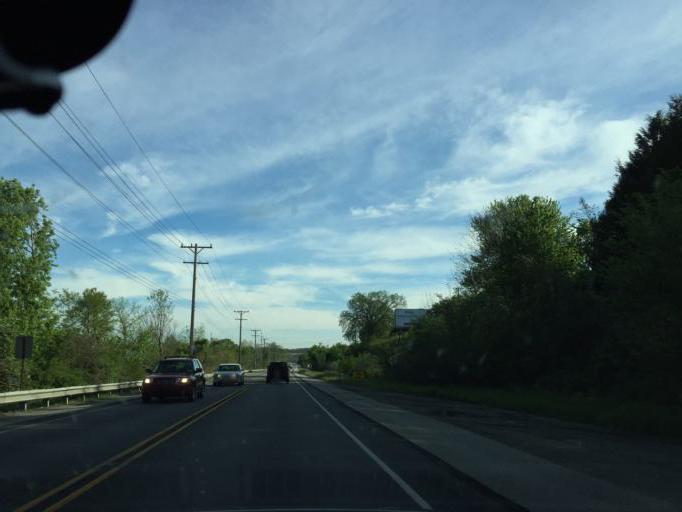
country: US
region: Pennsylvania
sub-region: Westmoreland County
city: Lawson Heights
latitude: 40.2999
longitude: -79.3940
